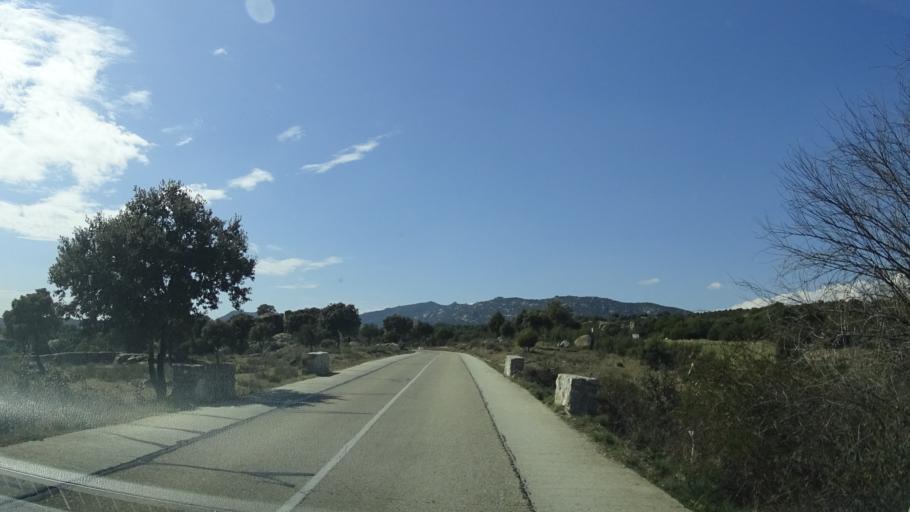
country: ES
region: Madrid
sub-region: Provincia de Madrid
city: Hoyo de Manzanares
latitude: 40.6328
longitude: -3.8621
